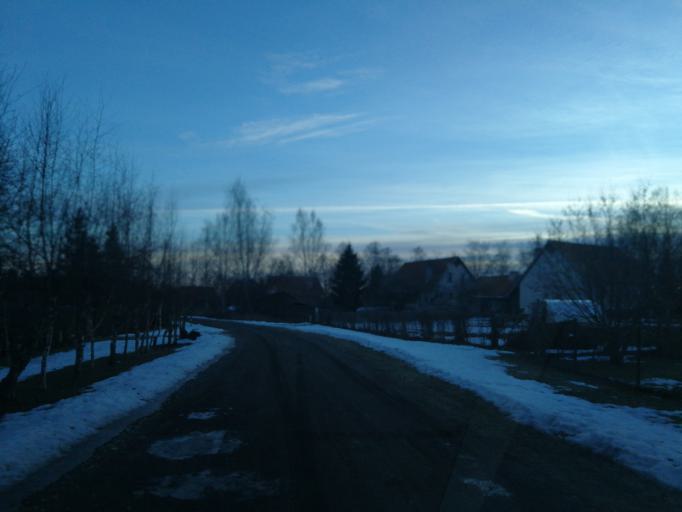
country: LV
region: Adazi
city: Adazi
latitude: 57.0924
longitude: 24.3156
